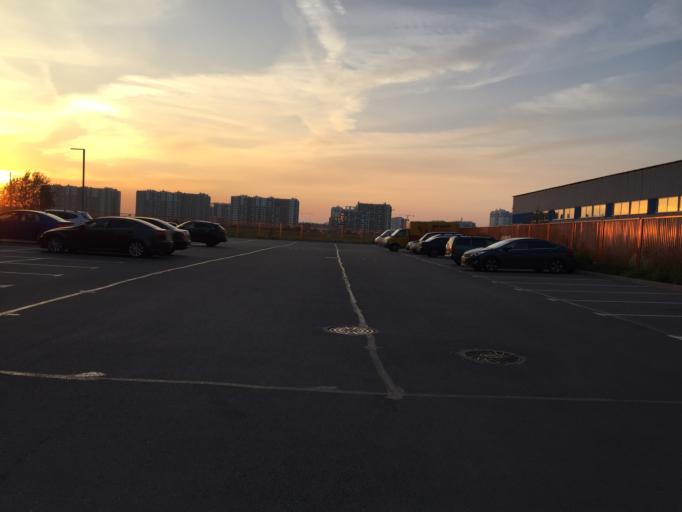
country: RU
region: St.-Petersburg
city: Grazhdanka
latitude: 60.0597
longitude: 30.4166
